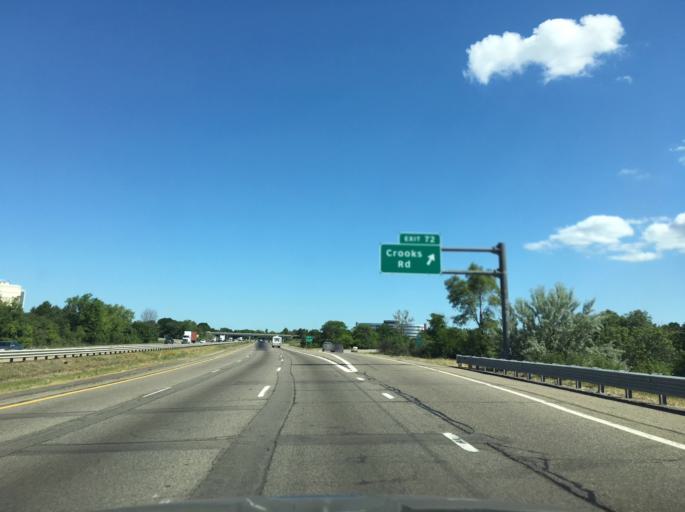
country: US
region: Michigan
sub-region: Oakland County
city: Troy
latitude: 42.5953
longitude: -83.1599
